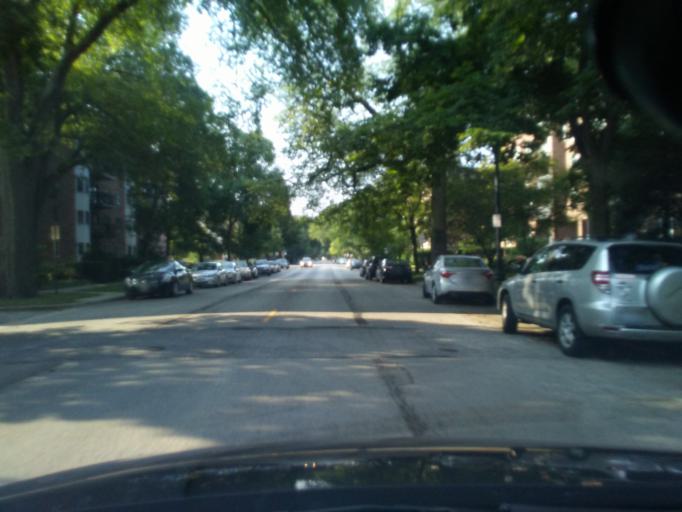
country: US
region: Illinois
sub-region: Cook County
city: Evanston
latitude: 42.0453
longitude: -87.6869
